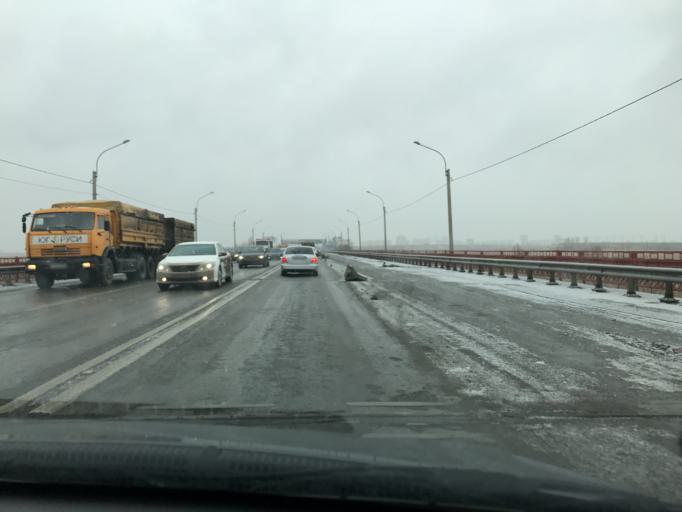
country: RU
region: Rostov
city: Bataysk
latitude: 47.1775
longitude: 39.7414
